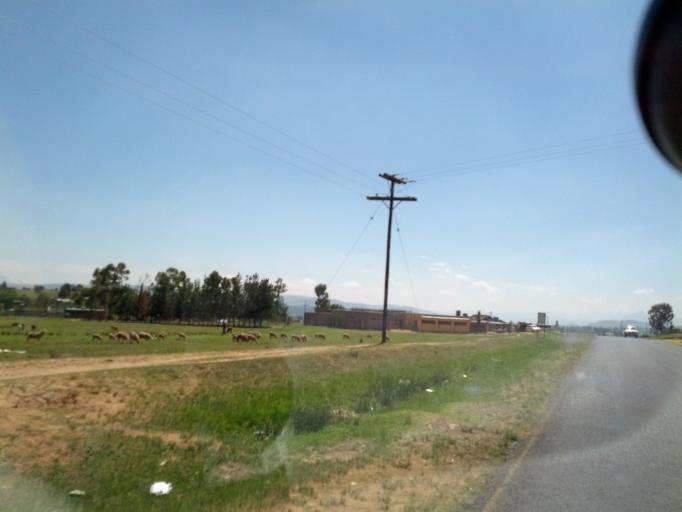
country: LS
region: Butha-Buthe
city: Butha-Buthe
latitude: -28.7791
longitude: 28.2297
